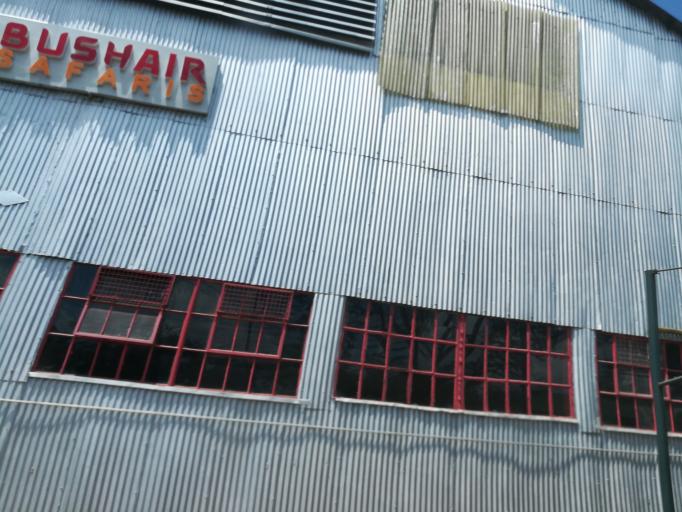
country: KE
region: Nairobi Area
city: Nairobi
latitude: -1.3195
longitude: 36.8108
